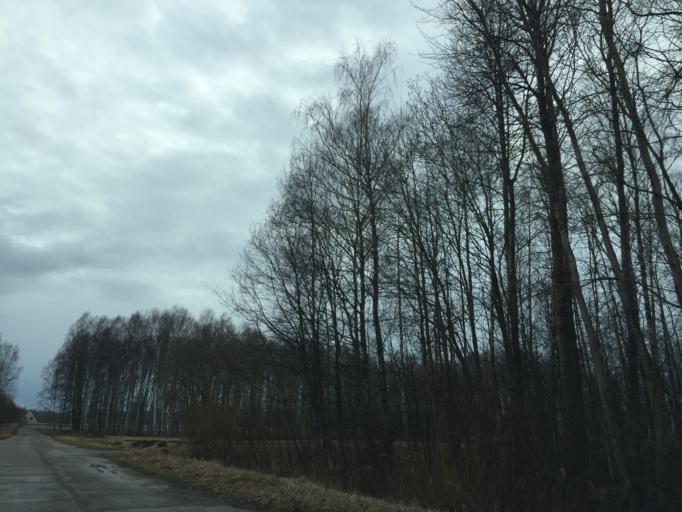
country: LV
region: Daugavpils
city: Daugavpils
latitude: 55.9394
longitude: 26.6547
